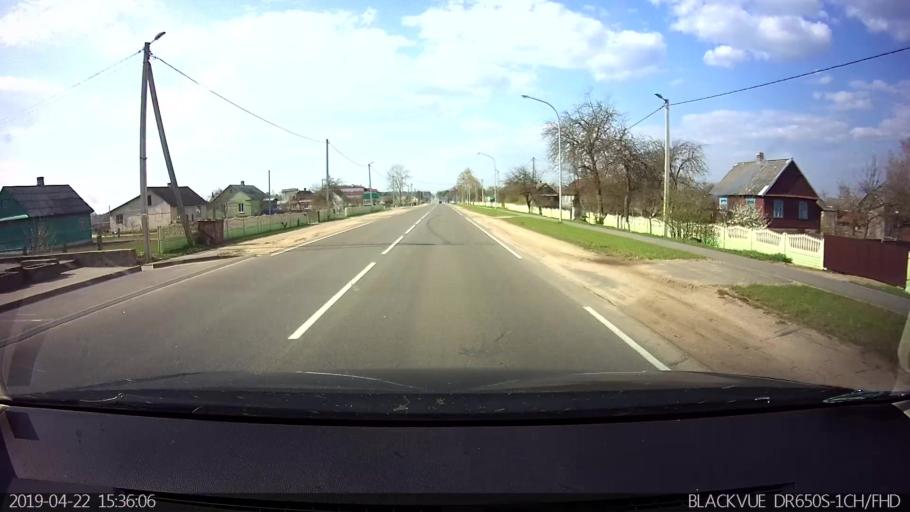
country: PL
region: Podlasie
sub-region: Powiat hajnowski
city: Czeremcha
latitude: 52.4542
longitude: 23.3683
